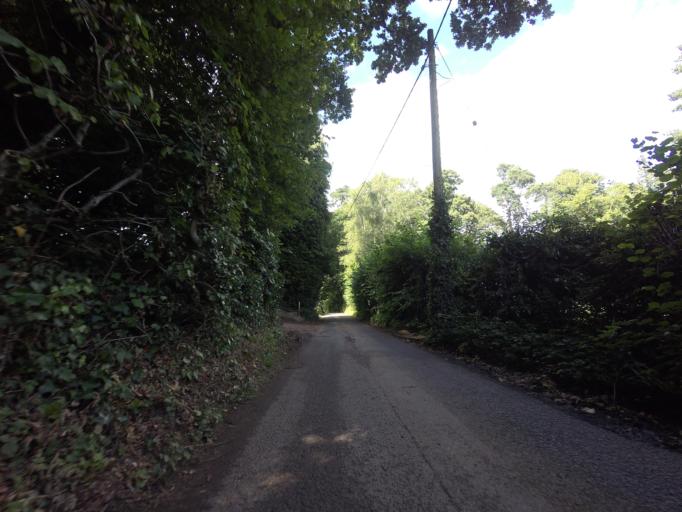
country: GB
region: England
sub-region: Kent
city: Borough Green
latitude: 51.2828
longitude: 0.2741
